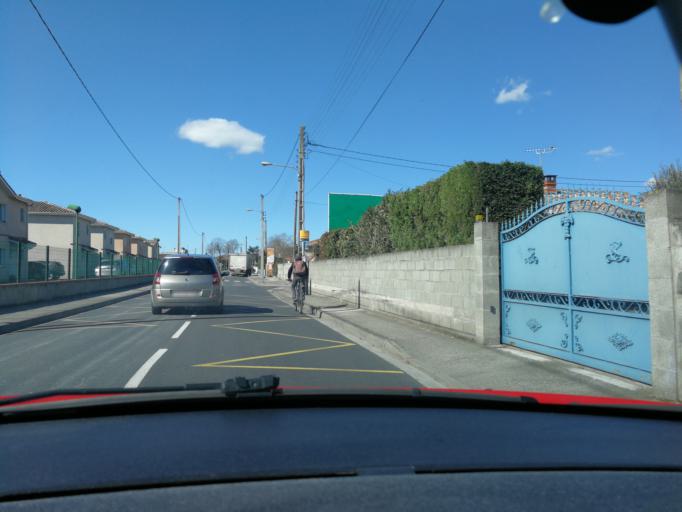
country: FR
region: Midi-Pyrenees
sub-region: Departement de la Haute-Garonne
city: Cugnaux
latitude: 43.5575
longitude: 1.3689
